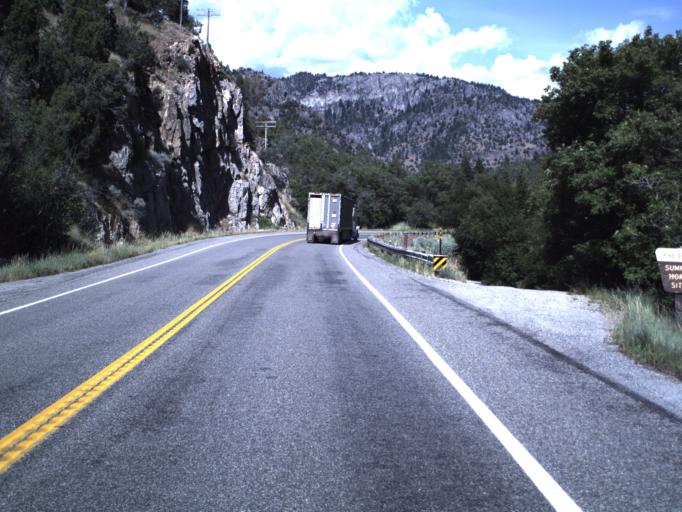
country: US
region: Utah
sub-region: Cache County
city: North Logan
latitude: 41.7691
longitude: -111.6612
